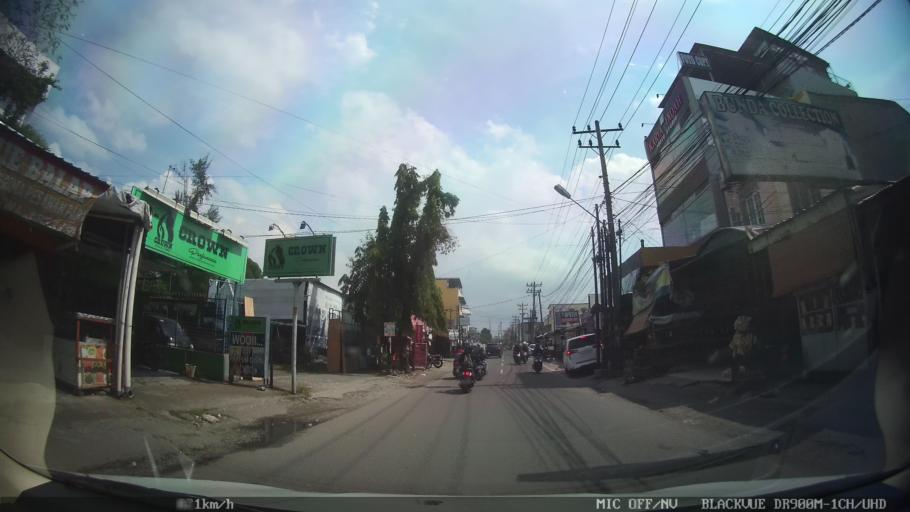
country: ID
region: North Sumatra
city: Medan
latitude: 3.6084
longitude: 98.6653
